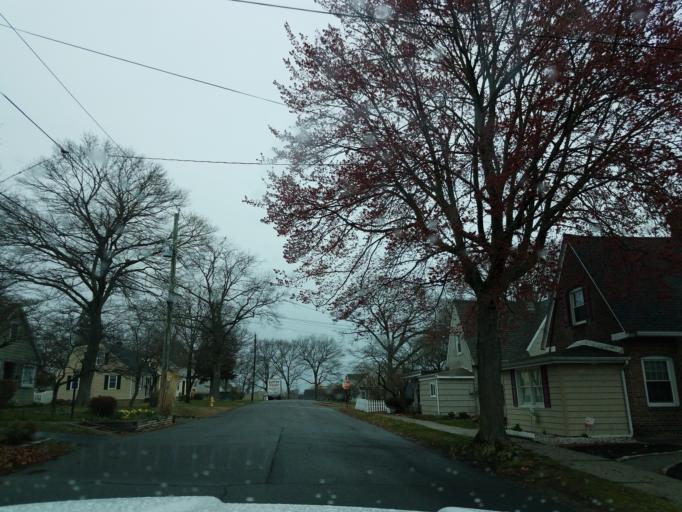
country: US
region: Connecticut
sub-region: Fairfield County
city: Stratford
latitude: 41.1569
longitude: -73.1261
